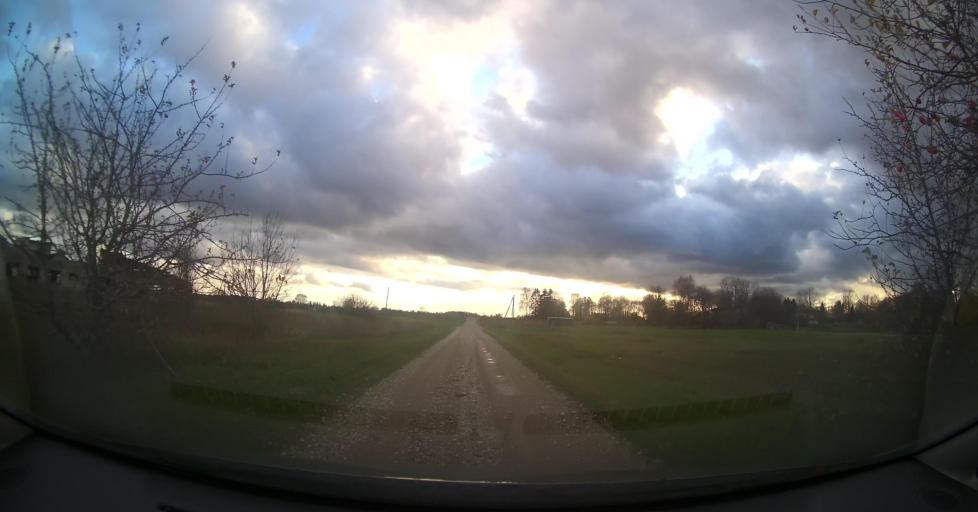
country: EE
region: Harju
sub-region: Raasiku vald
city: Arukula
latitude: 59.3484
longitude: 25.1038
